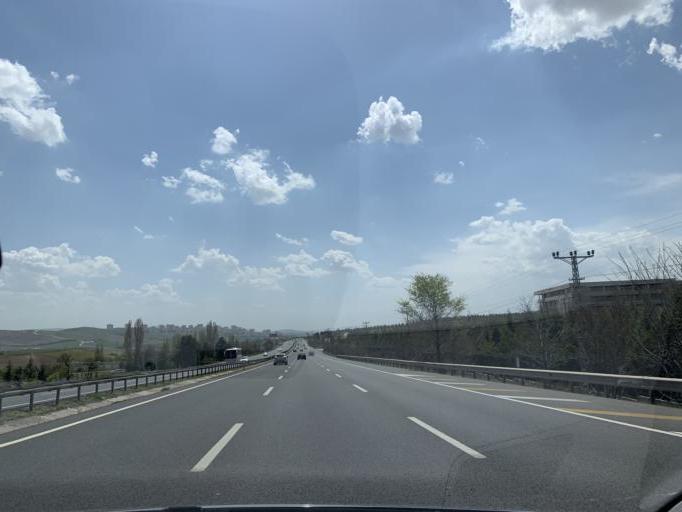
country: TR
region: Ankara
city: Etimesgut
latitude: 39.8476
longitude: 32.5969
